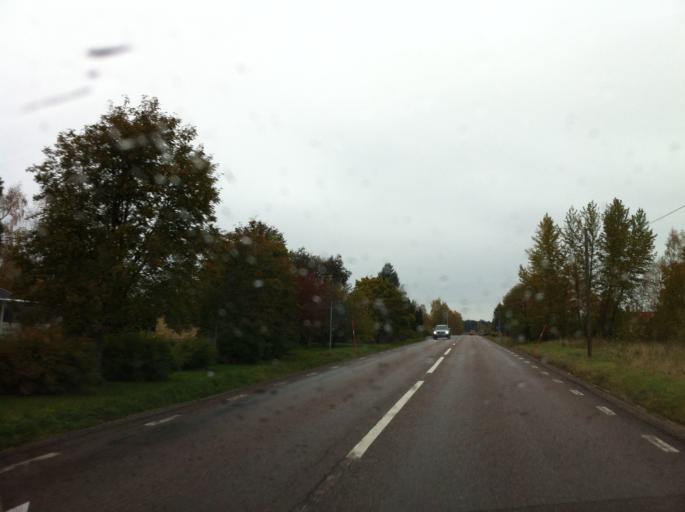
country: SE
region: Dalarna
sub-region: Ludvika Kommun
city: Grangesberg
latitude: 60.2487
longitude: 14.9788
